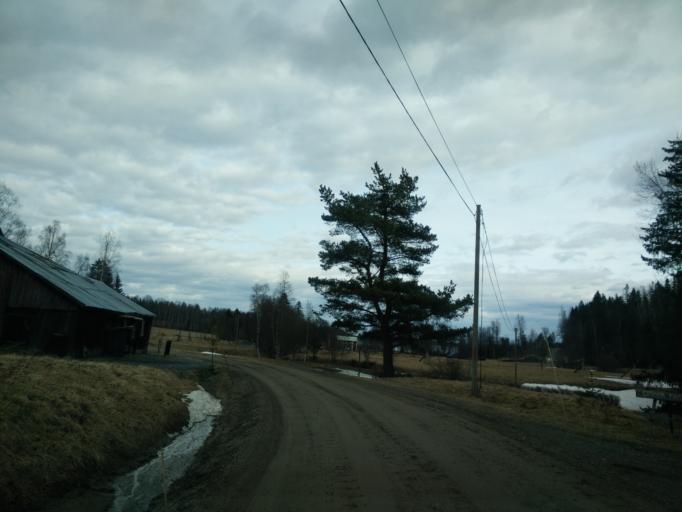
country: SE
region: Vaesternorrland
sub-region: Haernoesands Kommun
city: Haernoesand
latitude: 62.7447
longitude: 18.0703
